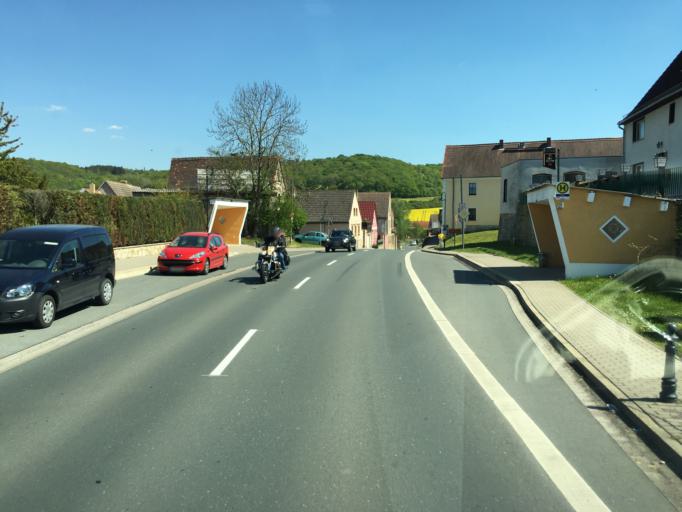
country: DE
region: Saxony-Anhalt
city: Balgstadt
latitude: 51.2053
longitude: 11.7322
